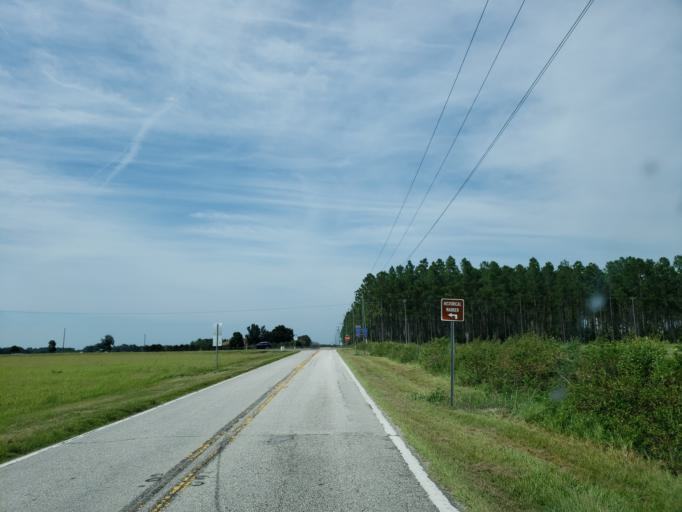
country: US
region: Florida
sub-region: Pasco County
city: San Antonio
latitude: 28.3749
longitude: -82.2786
